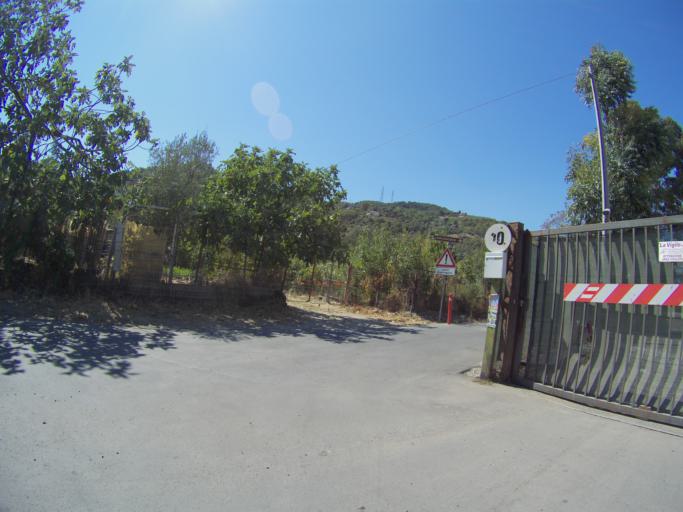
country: IT
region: Liguria
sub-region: Provincia di Imperia
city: Camporosso
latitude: 43.8213
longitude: 7.6311
